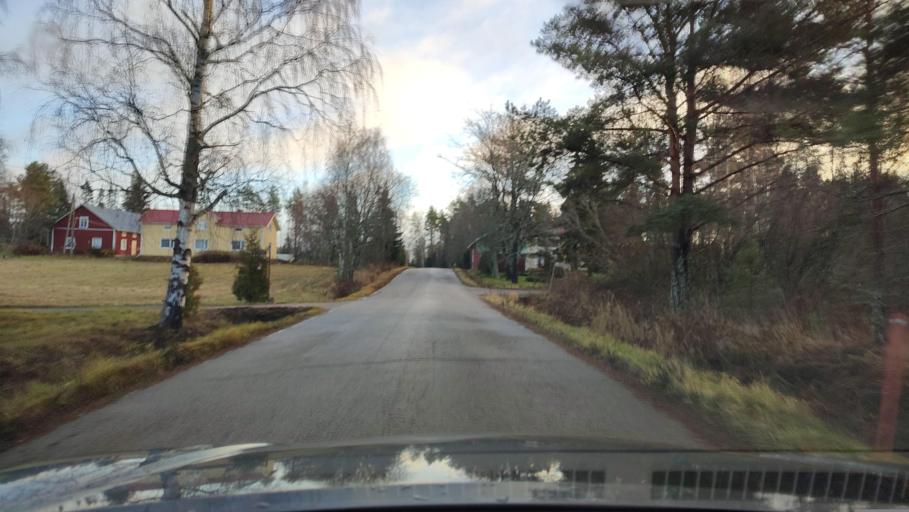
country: FI
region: Ostrobothnia
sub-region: Sydosterbotten
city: Naerpes
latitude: 62.4429
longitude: 21.3793
